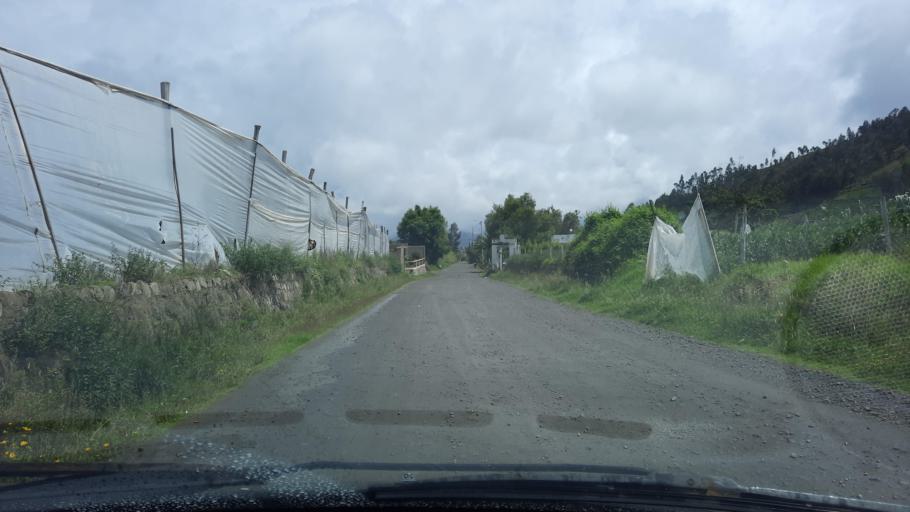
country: EC
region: Chimborazo
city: Riobamba
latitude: -1.6902
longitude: -78.6674
